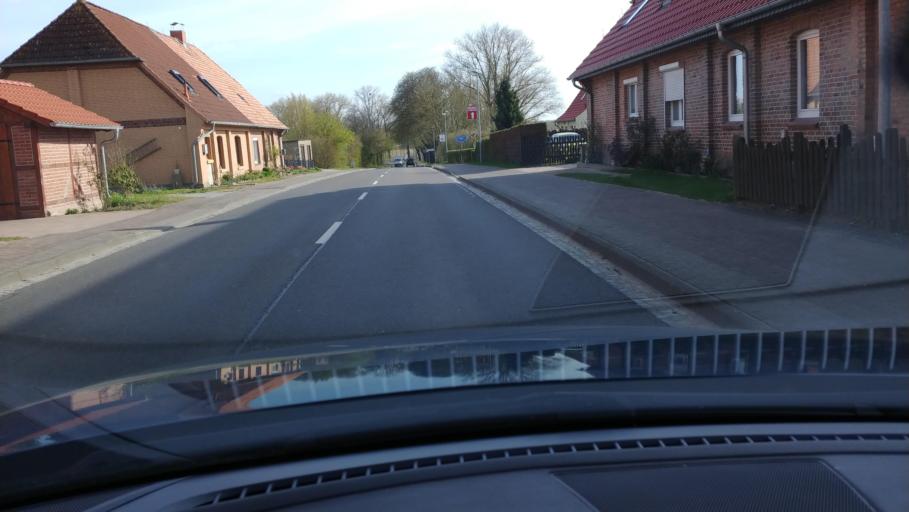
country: DE
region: Mecklenburg-Vorpommern
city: Seehof
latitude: 53.6893
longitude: 11.3957
